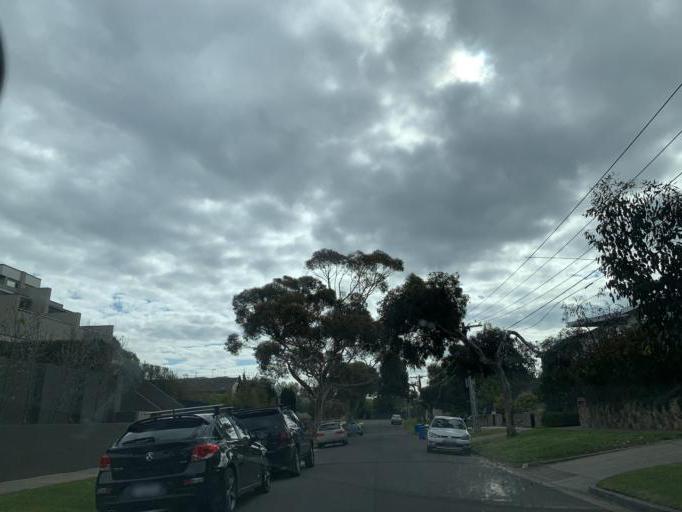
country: AU
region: Victoria
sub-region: Bayside
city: Black Rock
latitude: -37.9819
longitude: 145.0223
